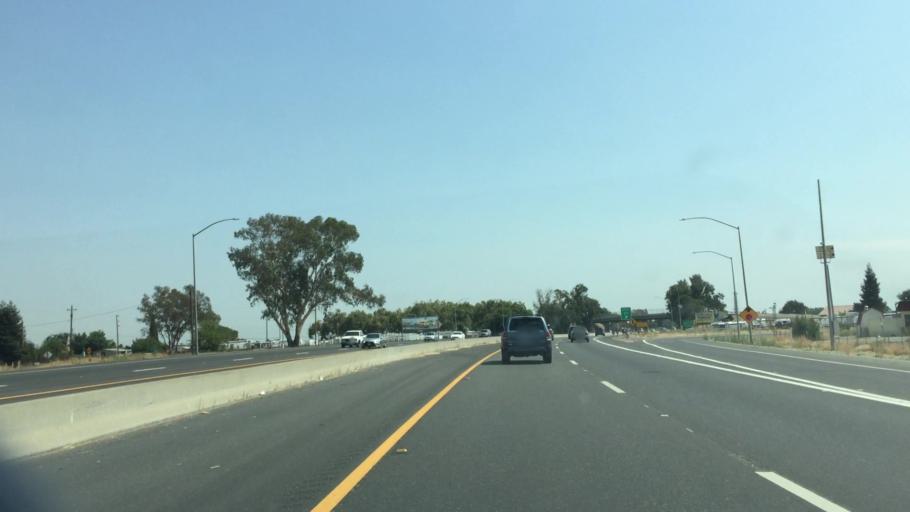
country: US
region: California
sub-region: San Joaquin County
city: Collierville
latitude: 38.2077
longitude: -121.2641
